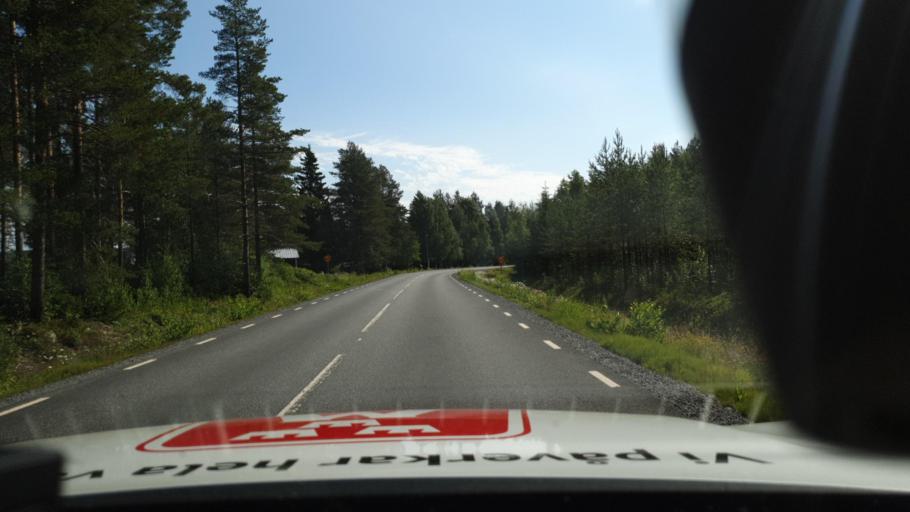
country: SE
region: Norrbotten
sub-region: Bodens Kommun
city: Saevast
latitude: 65.8382
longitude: 21.8348
